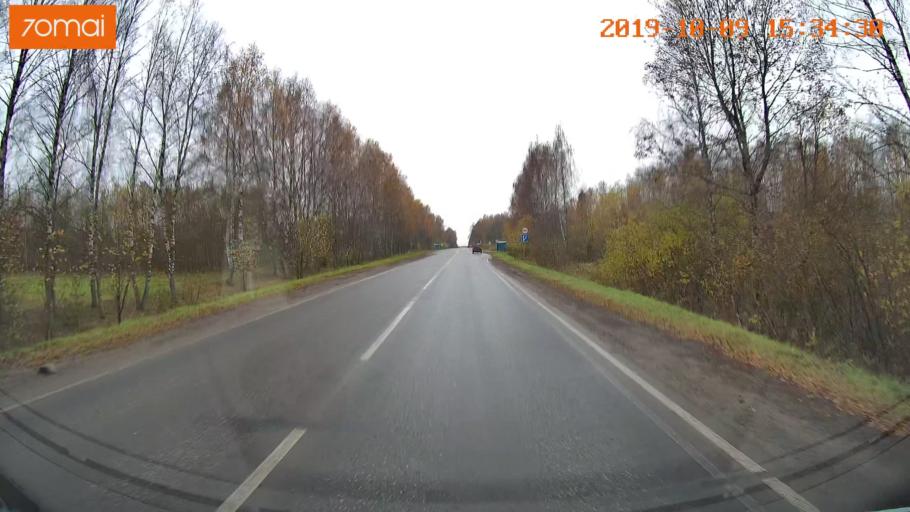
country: RU
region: Kostroma
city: Oktyabr'skiy
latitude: 57.9401
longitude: 41.2434
